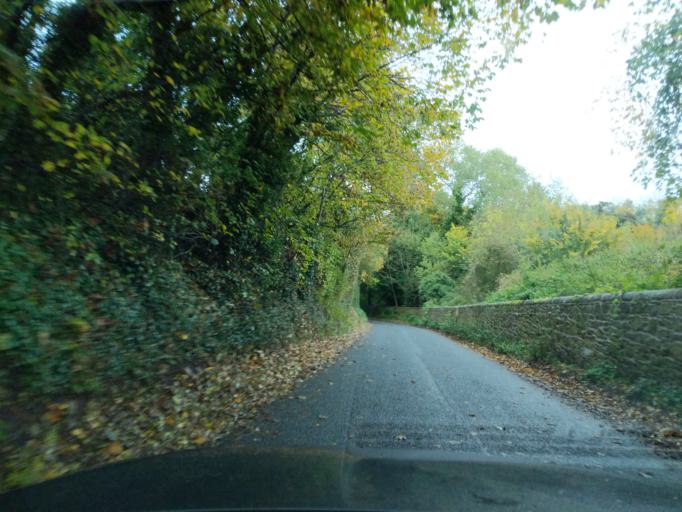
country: GB
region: Scotland
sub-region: East Lothian
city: Dunbar
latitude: 55.9741
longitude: -2.5215
